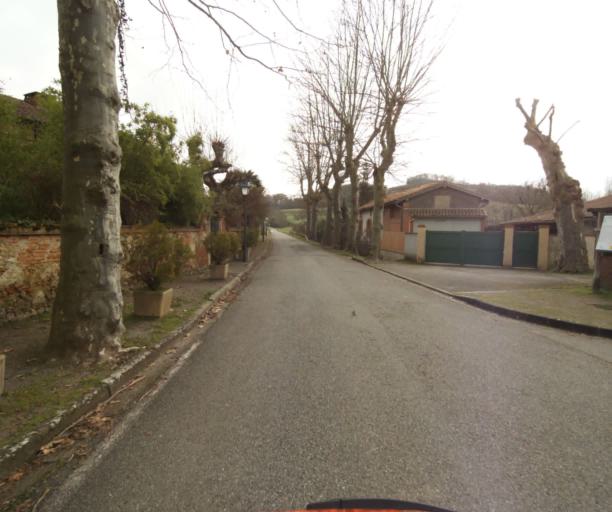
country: FR
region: Midi-Pyrenees
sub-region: Departement de la Haute-Garonne
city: Gaillac-Toulza
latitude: 43.1703
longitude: 1.4966
